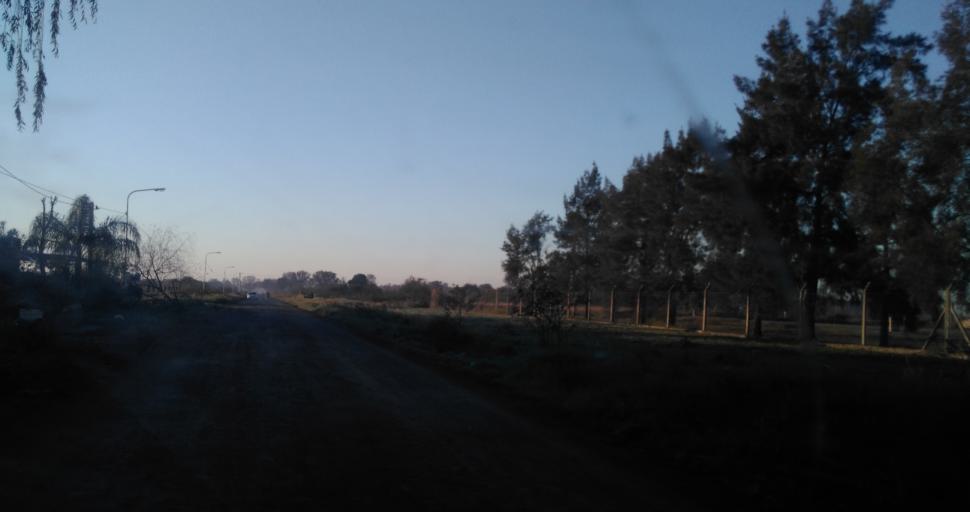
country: AR
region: Chaco
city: Fontana
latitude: -27.4321
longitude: -59.0367
